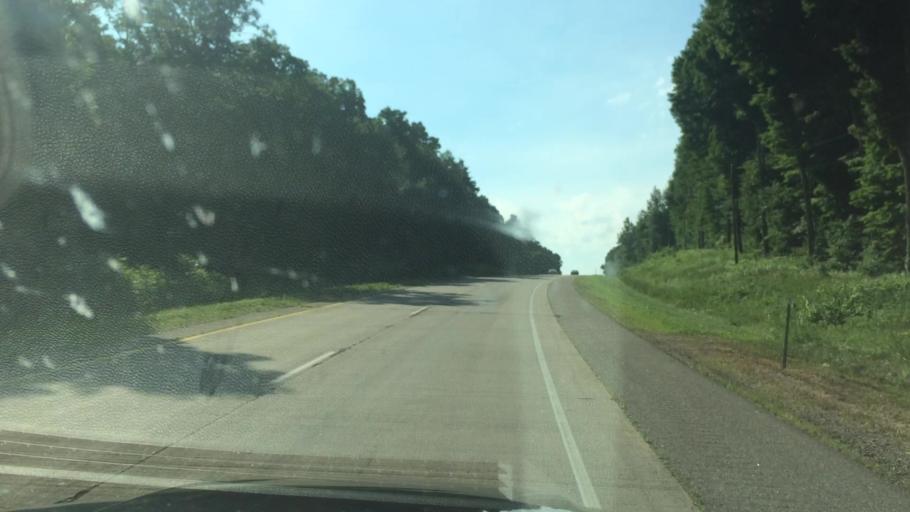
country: US
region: Wisconsin
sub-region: Shawano County
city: Wittenberg
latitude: 44.8230
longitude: -89.0594
